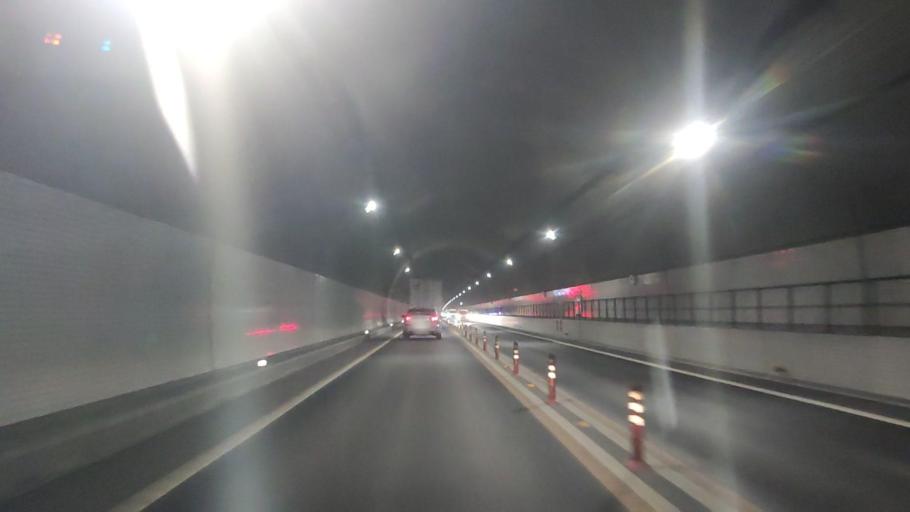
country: JP
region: Fukuoka
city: Kanda
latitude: 33.7608
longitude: 130.9609
